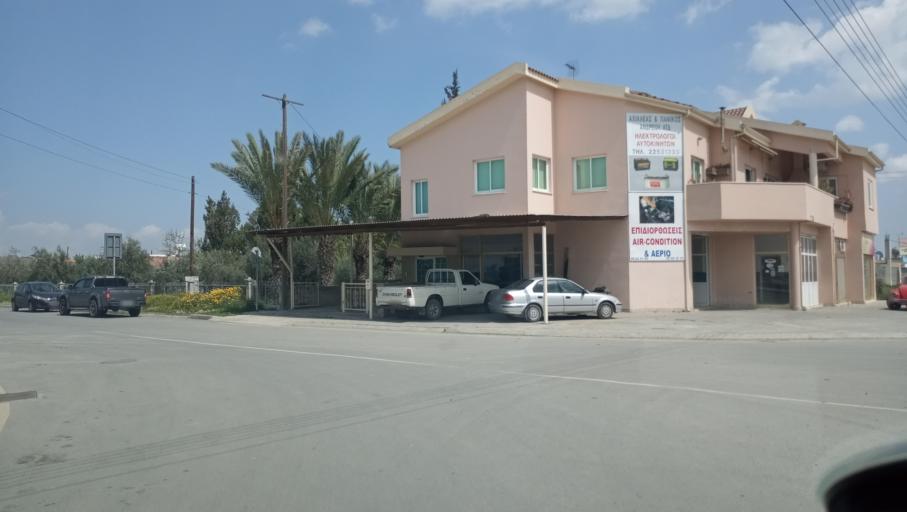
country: CY
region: Lefkosia
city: Dali
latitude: 35.0153
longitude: 33.3988
